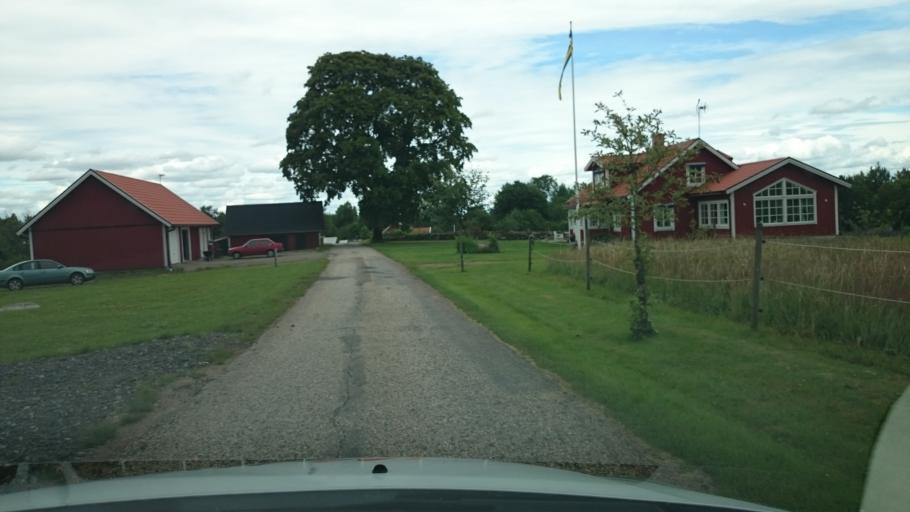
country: SE
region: Halland
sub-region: Hylte Kommun
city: Hyltebruk
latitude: 56.9651
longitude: 13.1961
